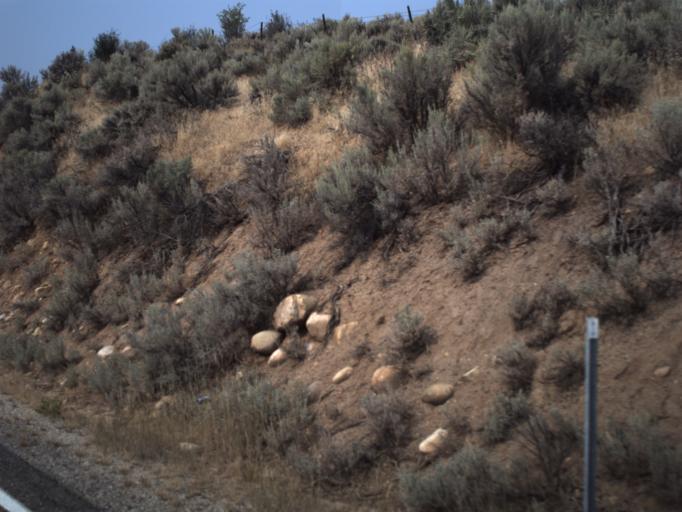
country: US
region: Utah
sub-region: Morgan County
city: Morgan
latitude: 40.9847
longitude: -111.5375
